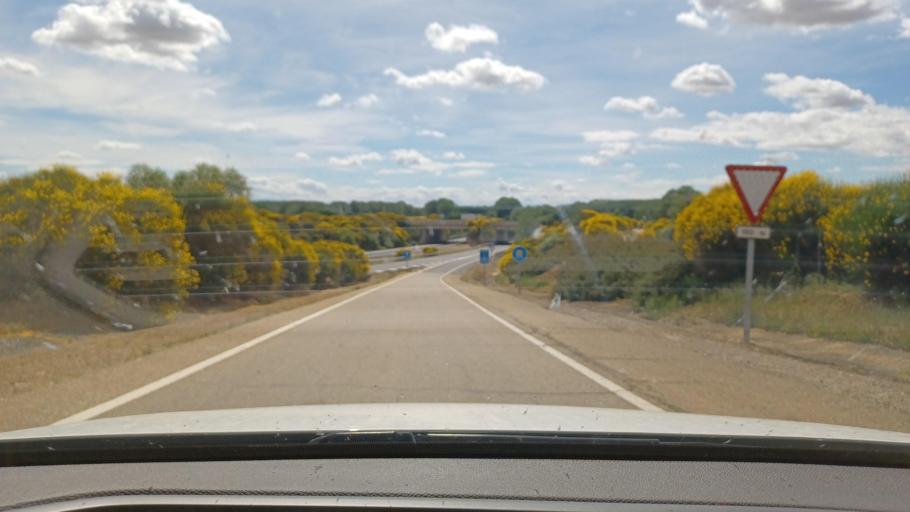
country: ES
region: Castille and Leon
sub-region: Provincia de Leon
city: Sahagun
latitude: 42.3847
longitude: -5.0280
